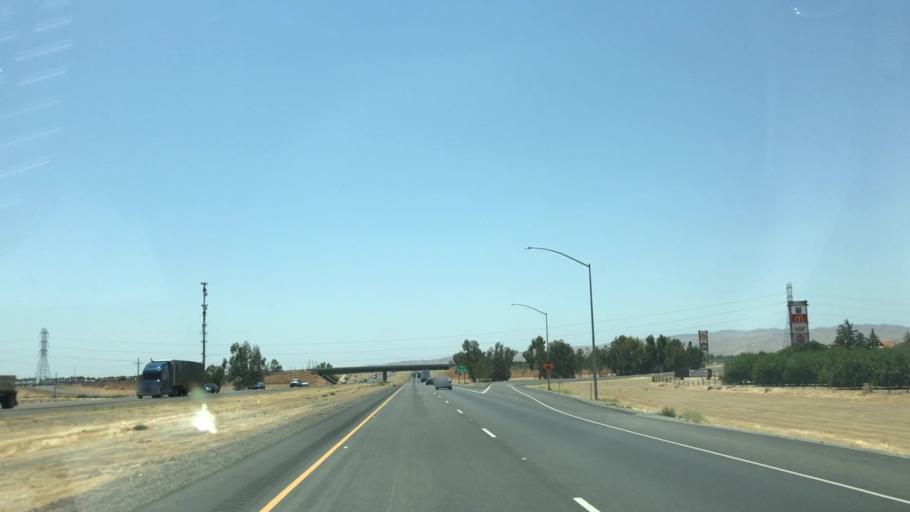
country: US
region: California
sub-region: Fresno County
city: Mendota
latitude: 36.6426
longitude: -120.6254
